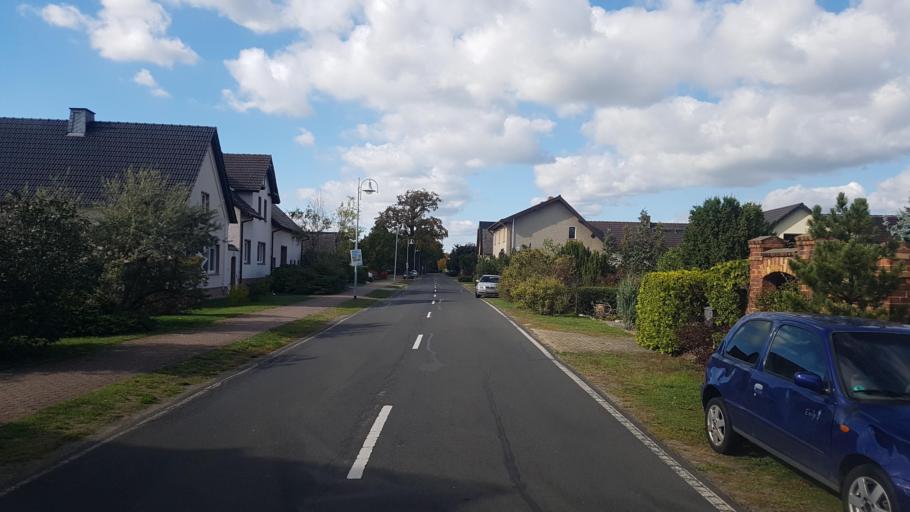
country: DE
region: Brandenburg
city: Peitz
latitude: 51.8097
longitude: 14.4254
